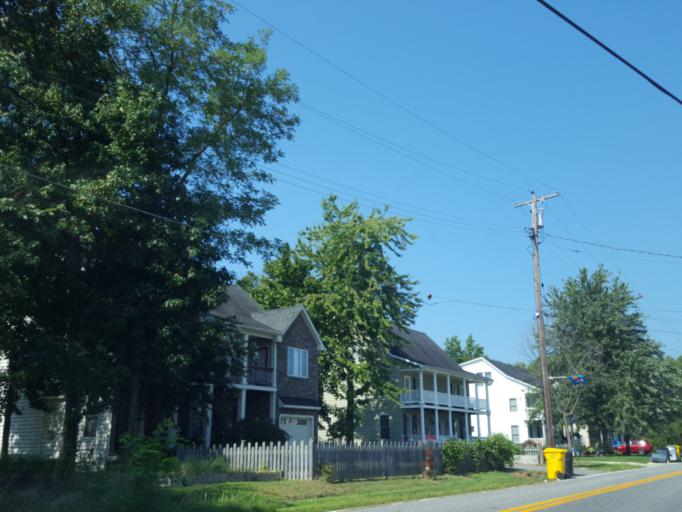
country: US
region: Maryland
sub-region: Anne Arundel County
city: Shady Side
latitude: 38.8427
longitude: -76.5402
